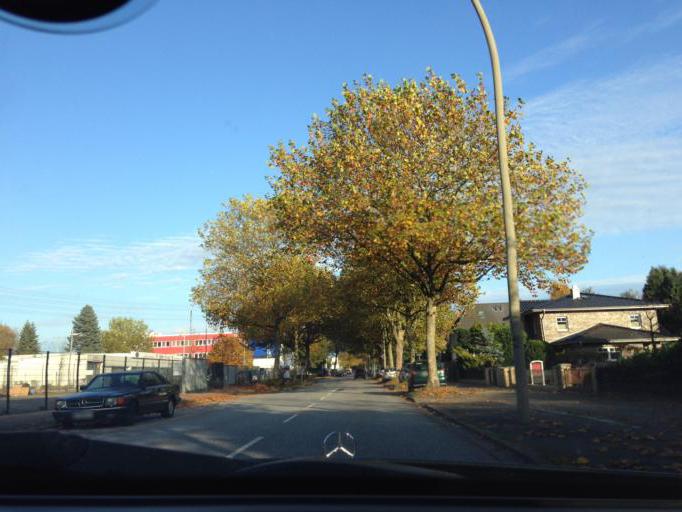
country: DE
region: Hamburg
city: Wandsbek
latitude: 53.5771
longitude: 10.1159
